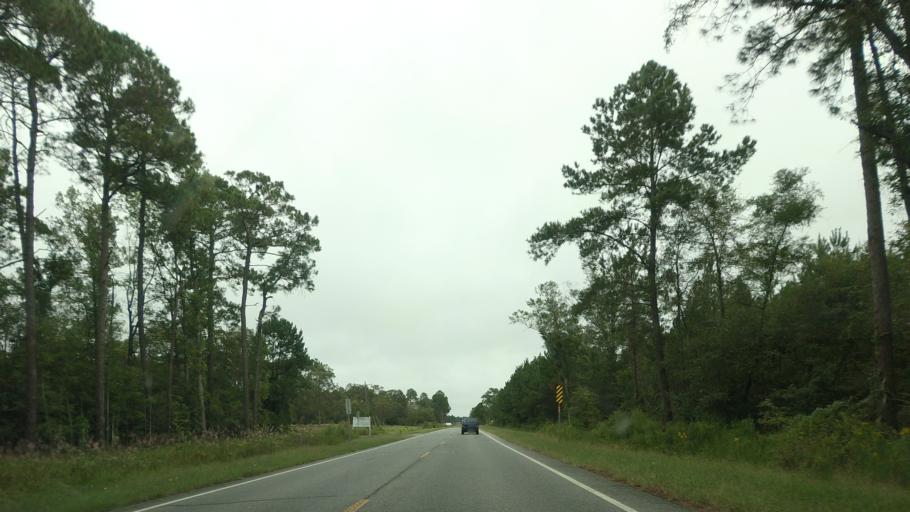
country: US
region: Georgia
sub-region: Irwin County
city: Ocilla
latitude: 31.5642
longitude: -83.2529
